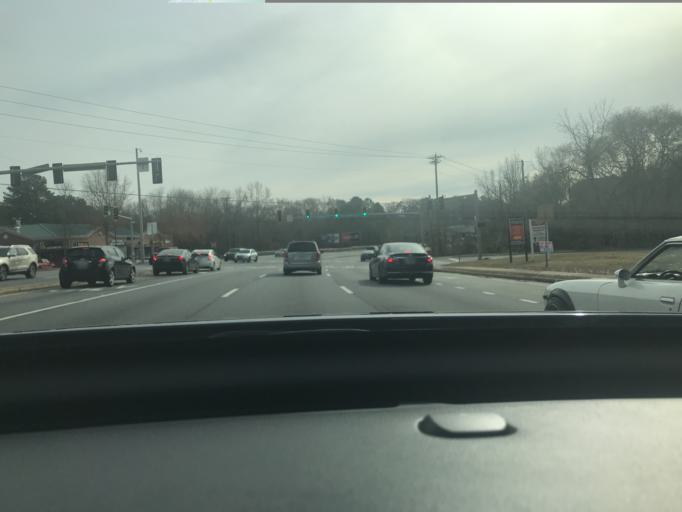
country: US
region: Georgia
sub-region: Gwinnett County
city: Lilburn
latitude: 33.9255
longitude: -84.1144
